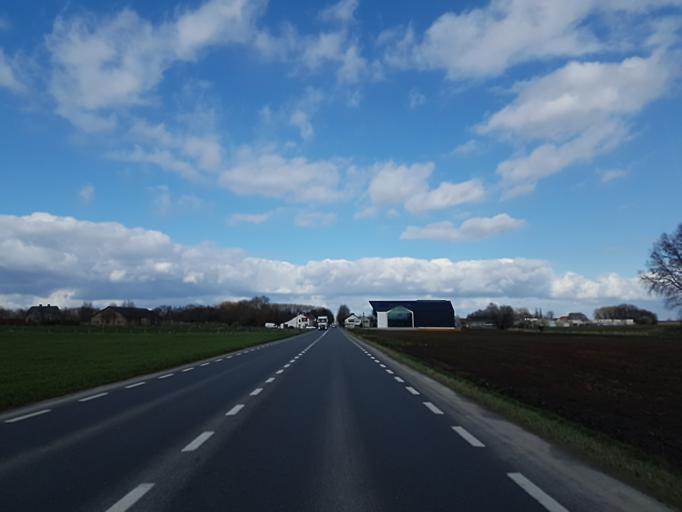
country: BE
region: Wallonia
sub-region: Province du Brabant Wallon
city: Perwez
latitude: 50.6439
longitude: 4.7894
